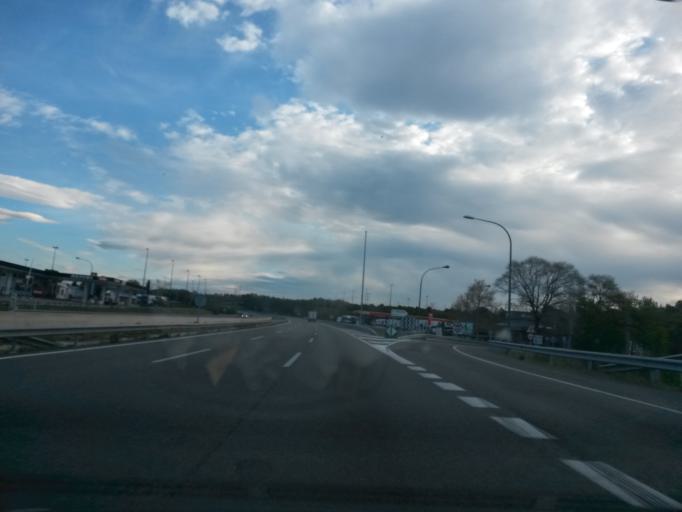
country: ES
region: Catalonia
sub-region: Provincia de Girona
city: Pontos
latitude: 42.1720
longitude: 2.9299
